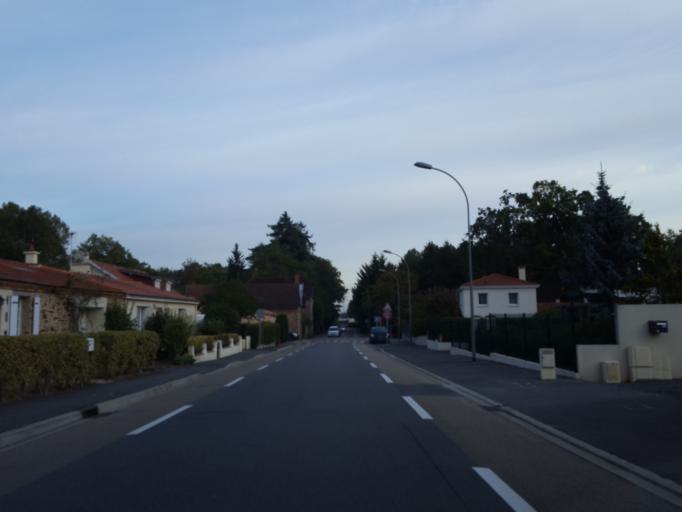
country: FR
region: Pays de la Loire
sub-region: Departement de la Loire-Atlantique
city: Basse-Goulaine
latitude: 47.1989
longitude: -1.4656
